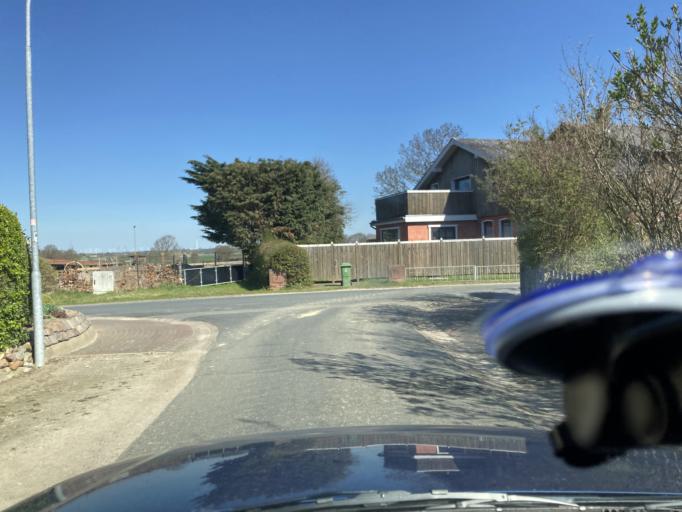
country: DE
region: Schleswig-Holstein
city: Nindorf
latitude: 54.0875
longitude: 9.1152
